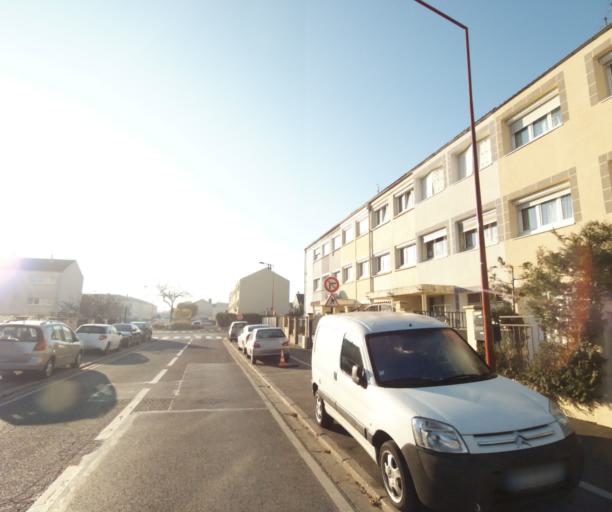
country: FR
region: Ile-de-France
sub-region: Departement du Val-d'Oise
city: Arnouville
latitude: 48.9979
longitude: 2.4276
